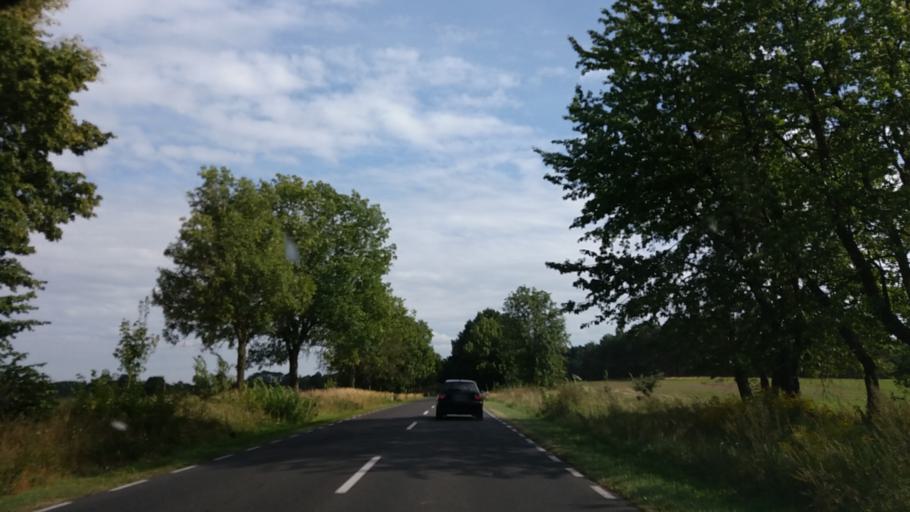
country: PL
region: West Pomeranian Voivodeship
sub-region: Powiat stargardzki
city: Suchan
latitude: 53.2129
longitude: 15.3141
